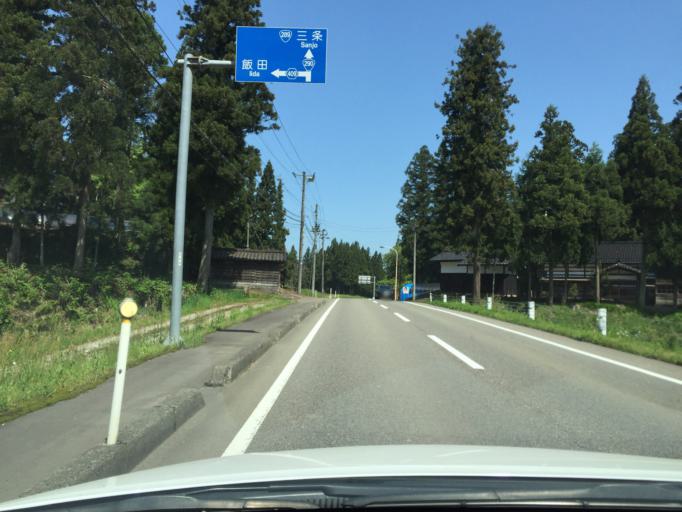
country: JP
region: Niigata
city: Kamo
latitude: 37.5787
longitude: 139.0728
